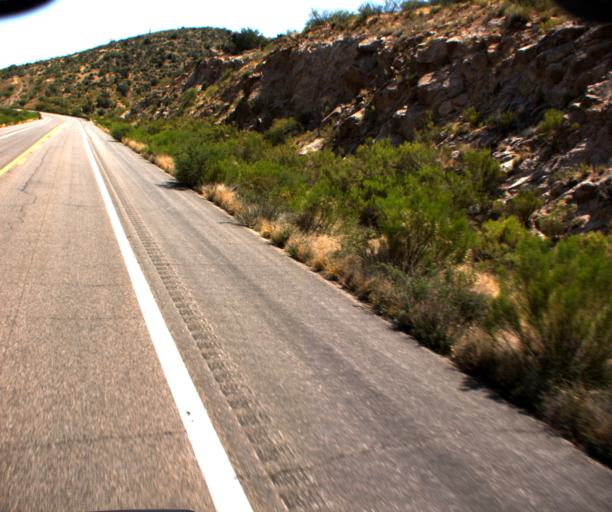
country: US
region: Arizona
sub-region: Gila County
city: Claypool
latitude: 33.5109
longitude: -110.8689
